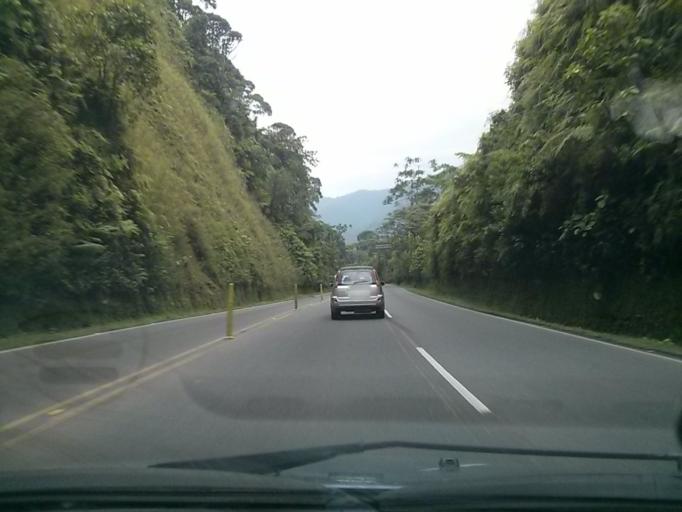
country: CR
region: San Jose
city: Dulce Nombre de Jesus
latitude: 10.1686
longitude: -83.9346
